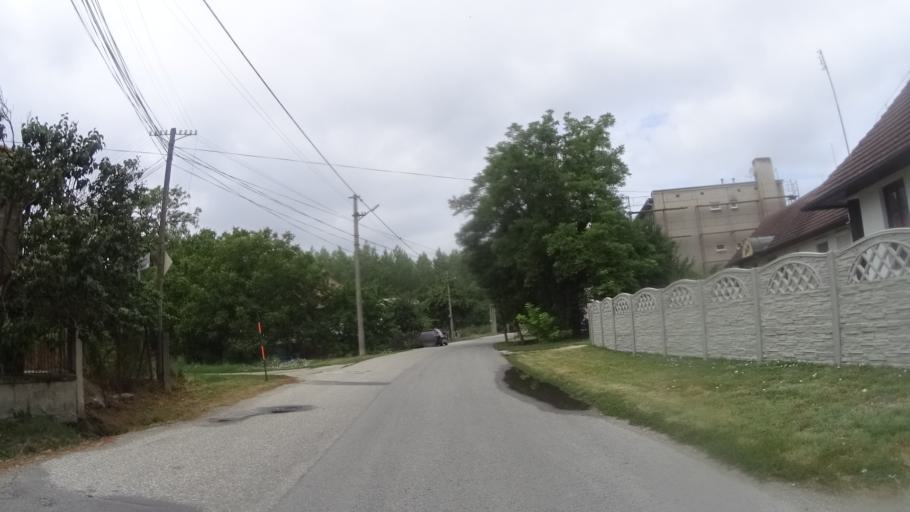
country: HU
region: Komarom-Esztergom
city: Acs
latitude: 47.7692
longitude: 17.9683
